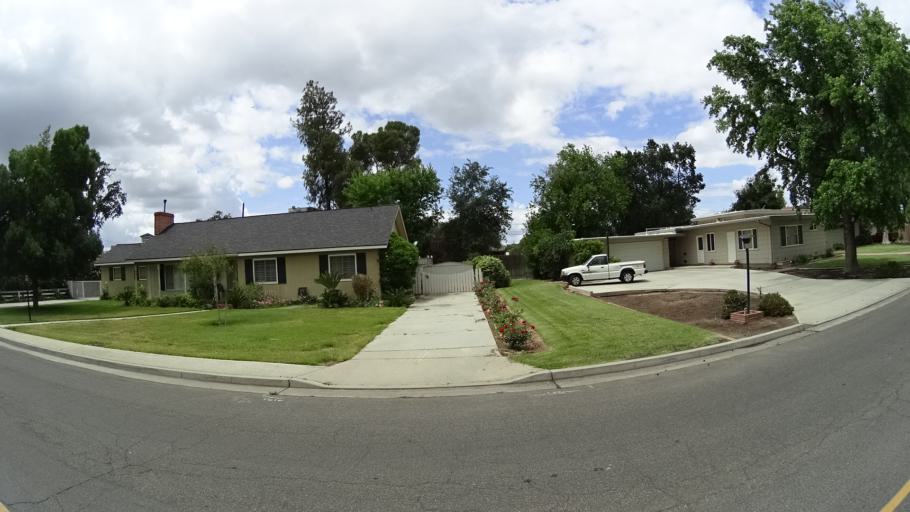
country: US
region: California
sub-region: Kings County
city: Hanford
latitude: 36.3438
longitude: -119.6517
